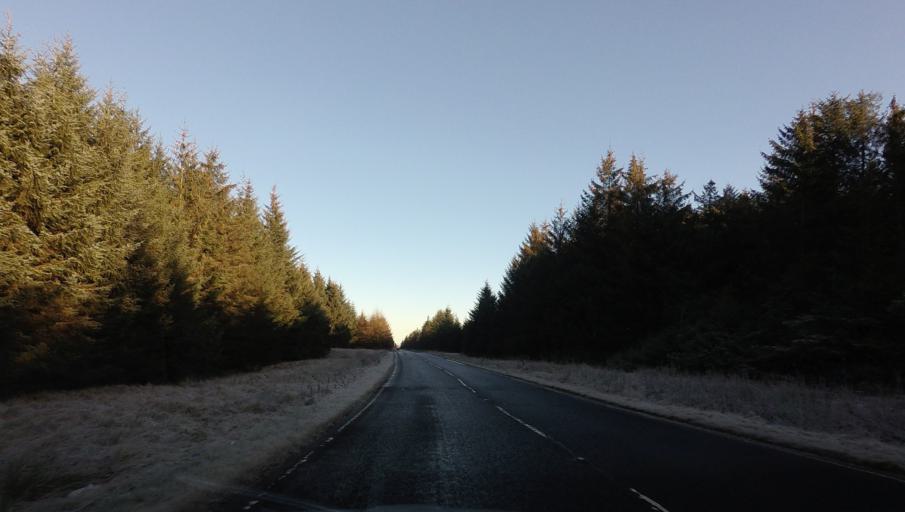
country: GB
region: Scotland
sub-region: West Lothian
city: Fauldhouse
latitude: 55.8136
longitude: -3.7046
